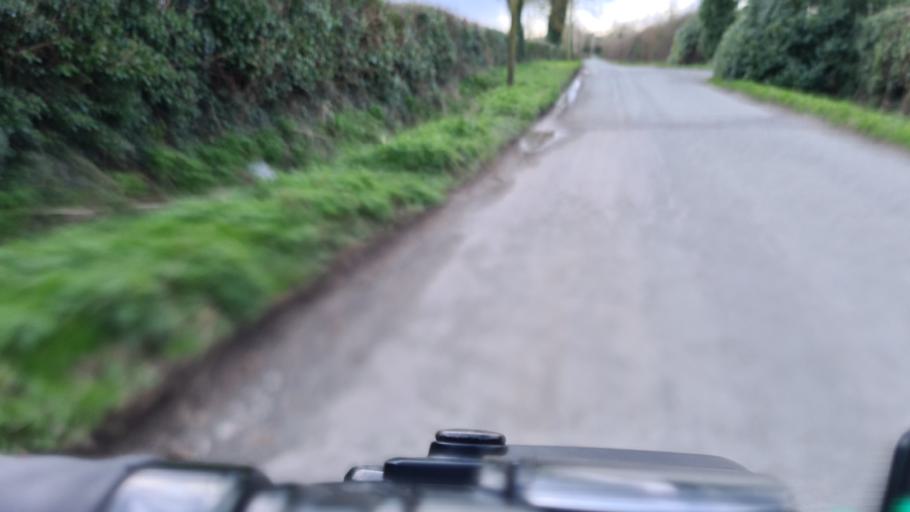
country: IE
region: Leinster
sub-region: Kildare
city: Celbridge
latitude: 53.3492
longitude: -6.5784
